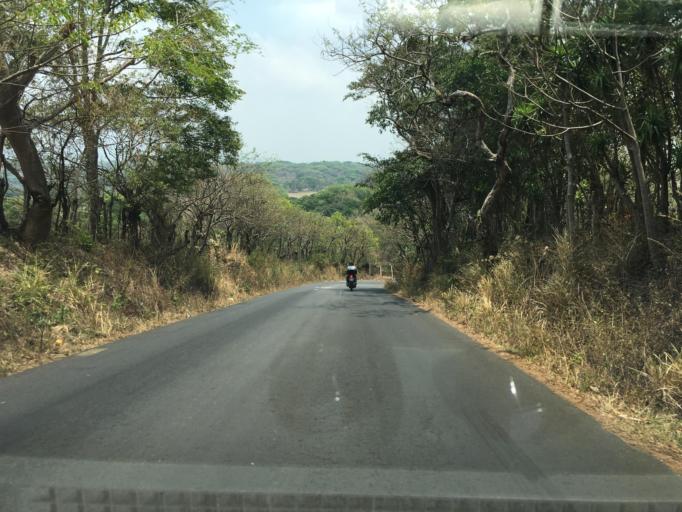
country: GT
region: Santa Rosa
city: Pueblo Nuevo Vinas
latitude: 14.3156
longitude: -90.5433
